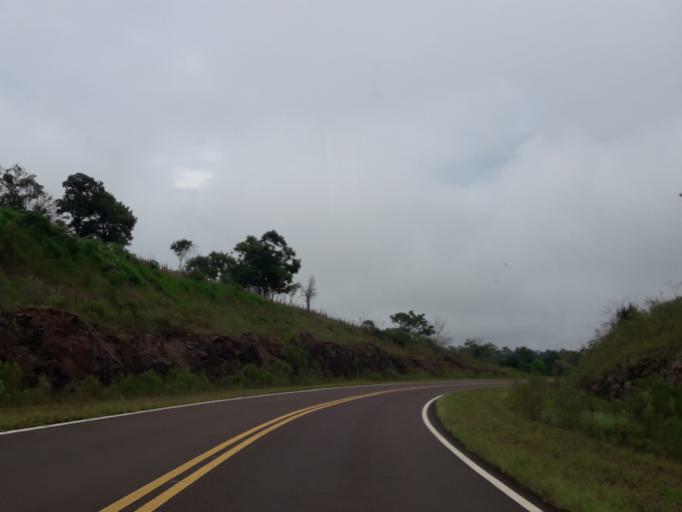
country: AR
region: Misiones
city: Bernardo de Irigoyen
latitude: -26.3961
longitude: -53.8087
